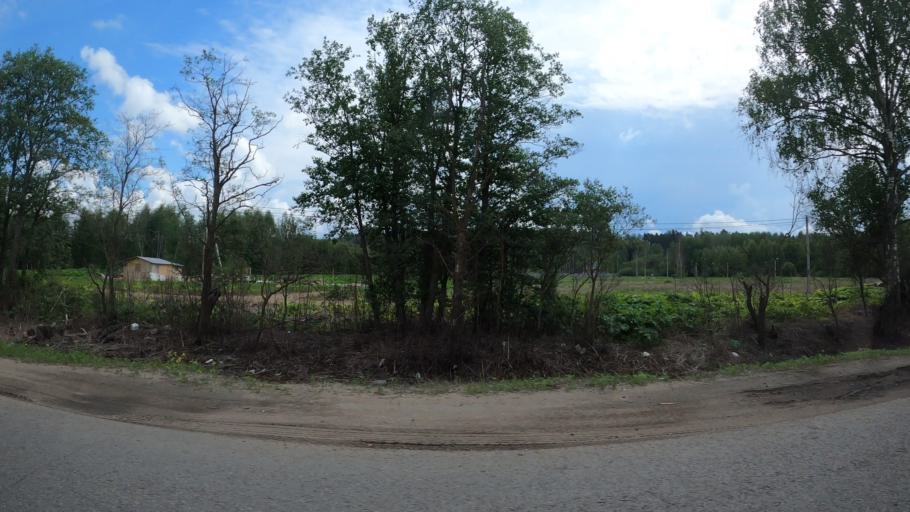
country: RU
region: Moskovskaya
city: Krasnoarmeysk
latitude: 56.0233
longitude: 38.1768
